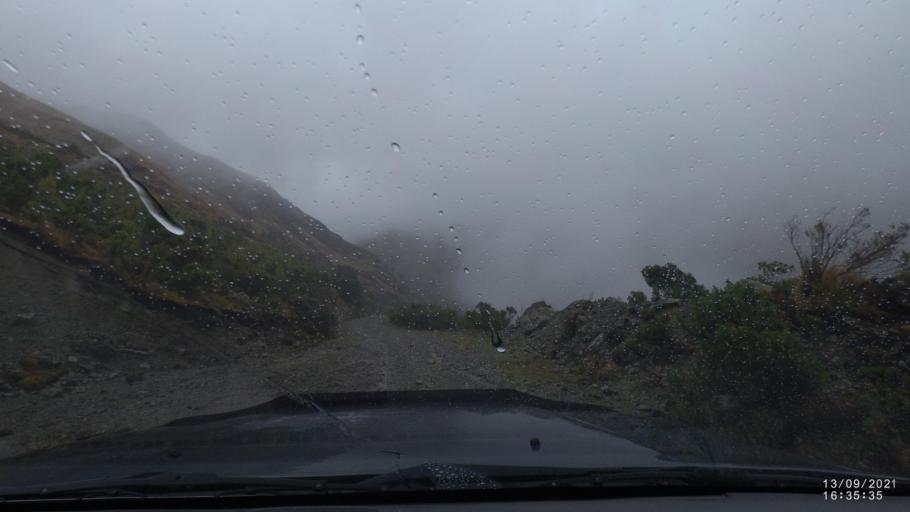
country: BO
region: Cochabamba
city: Colomi
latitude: -17.2792
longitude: -65.7127
